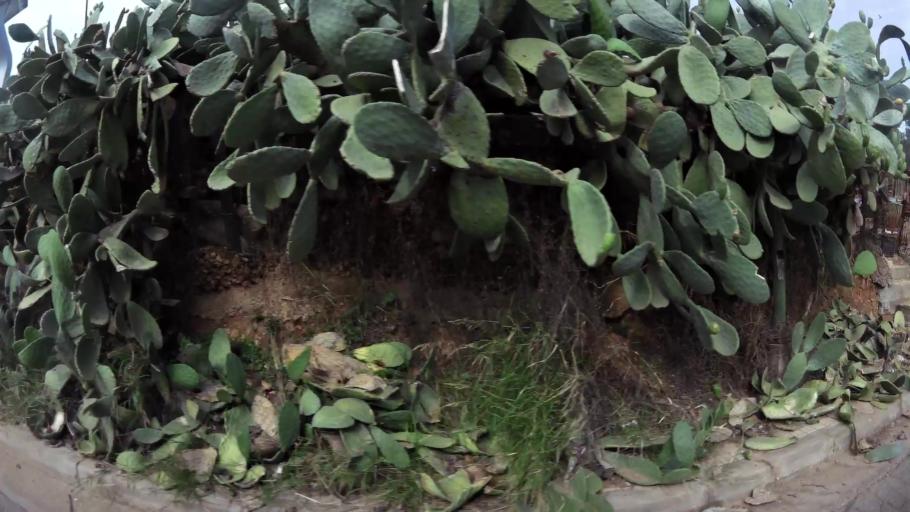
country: GR
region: Attica
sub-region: Nomarchia Athinas
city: Chaidari
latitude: 38.0261
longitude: 23.6708
